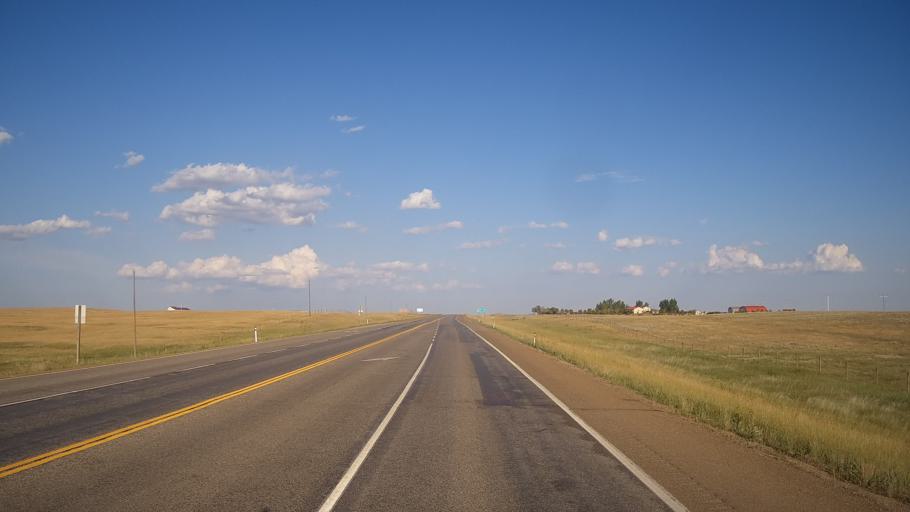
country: CA
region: Alberta
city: Hanna
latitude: 51.6303
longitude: -111.9177
